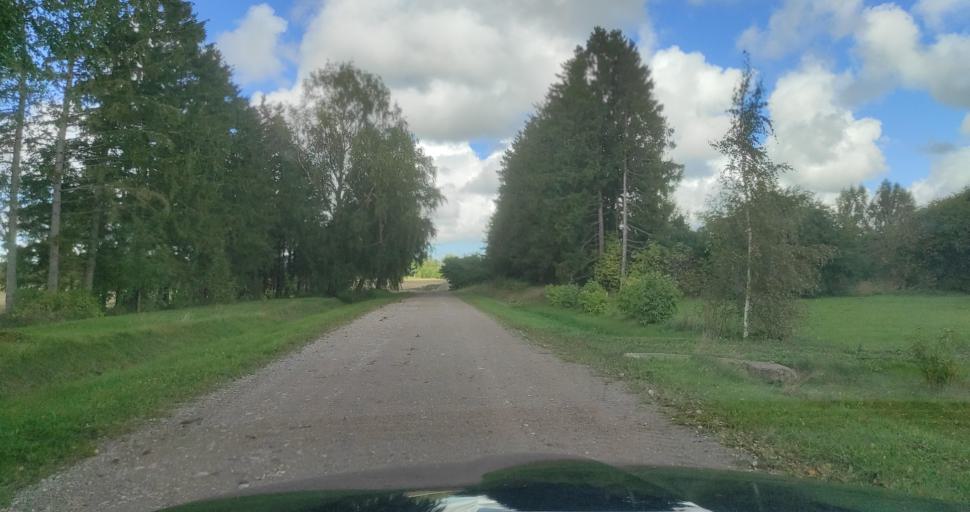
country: LV
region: Ventspils Rajons
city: Piltene
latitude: 57.2692
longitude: 21.5884
